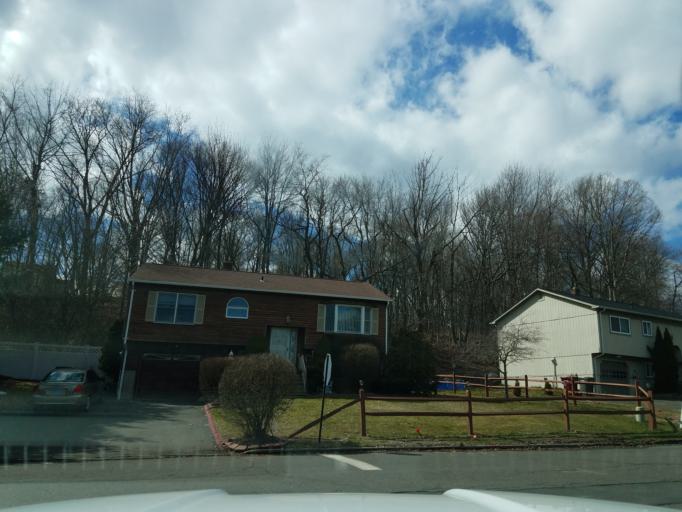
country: US
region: Connecticut
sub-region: New Haven County
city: Prospect
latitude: 41.4794
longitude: -73.0074
